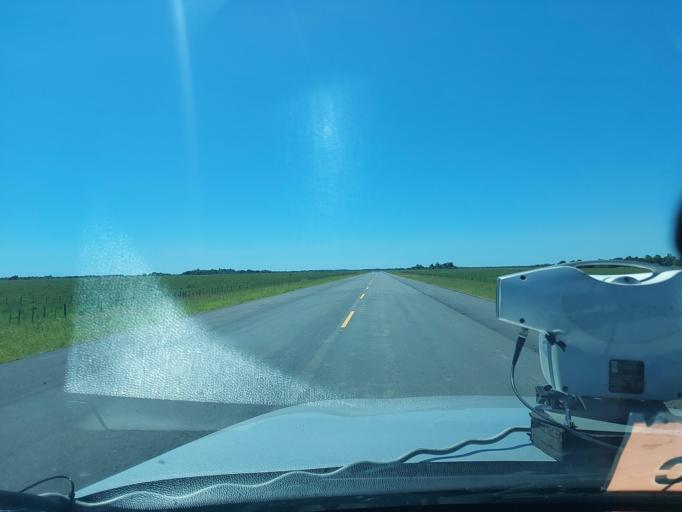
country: PY
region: Neembucu
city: Pilar
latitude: -26.8294
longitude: -58.2370
